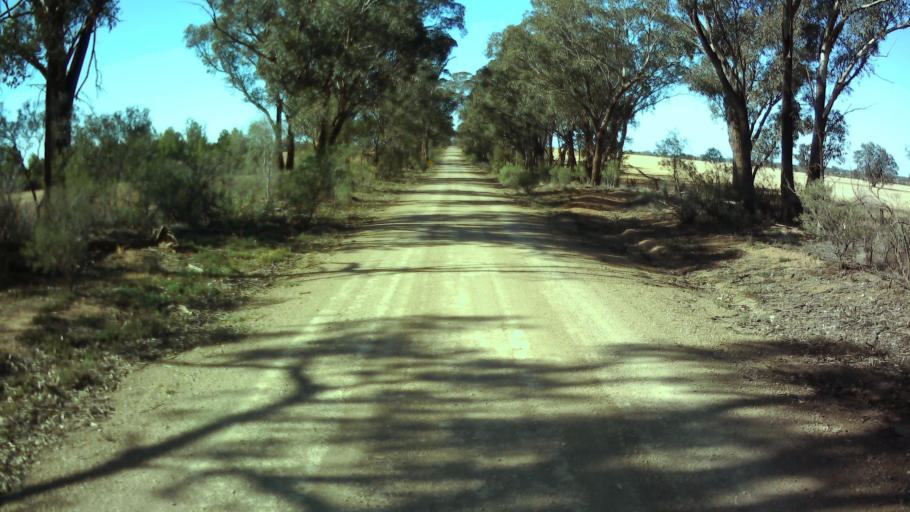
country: AU
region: New South Wales
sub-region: Weddin
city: Grenfell
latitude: -33.9036
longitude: 147.8781
